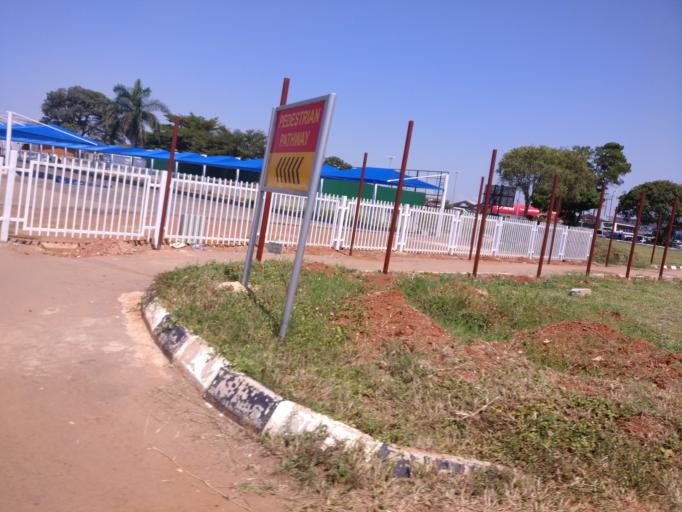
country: UG
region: Central Region
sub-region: Wakiso District
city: Entebbe
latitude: 0.0451
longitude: 32.4452
